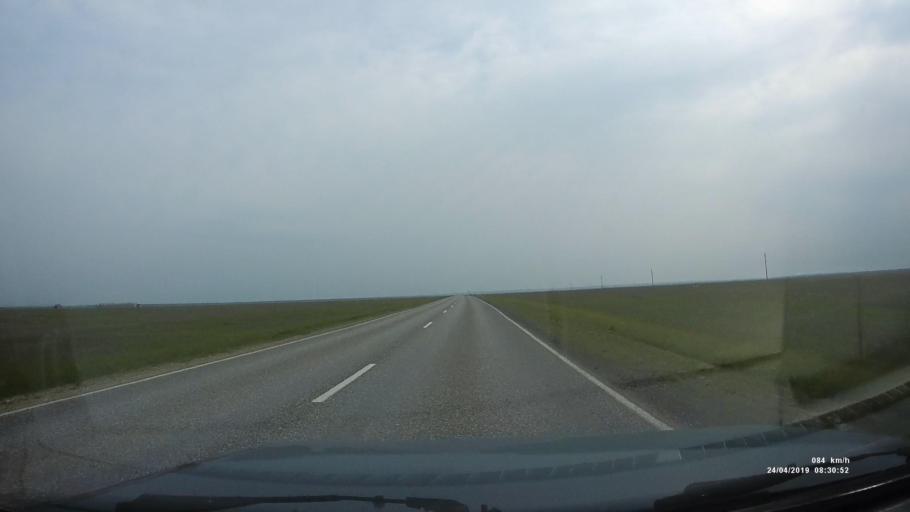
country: RU
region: Kalmykiya
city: Priyutnoye
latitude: 46.1626
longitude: 43.8520
